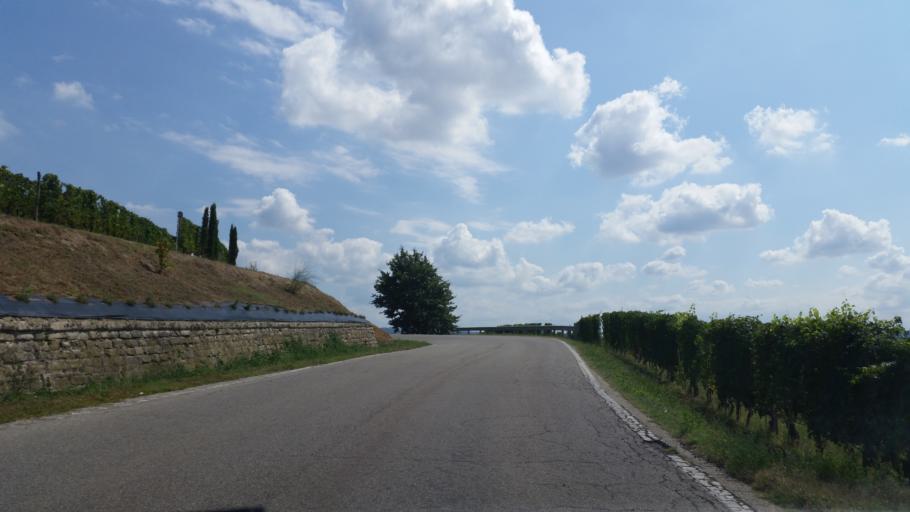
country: IT
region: Piedmont
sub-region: Provincia di Cuneo
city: Barbaresco
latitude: 44.7083
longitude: 8.0675
